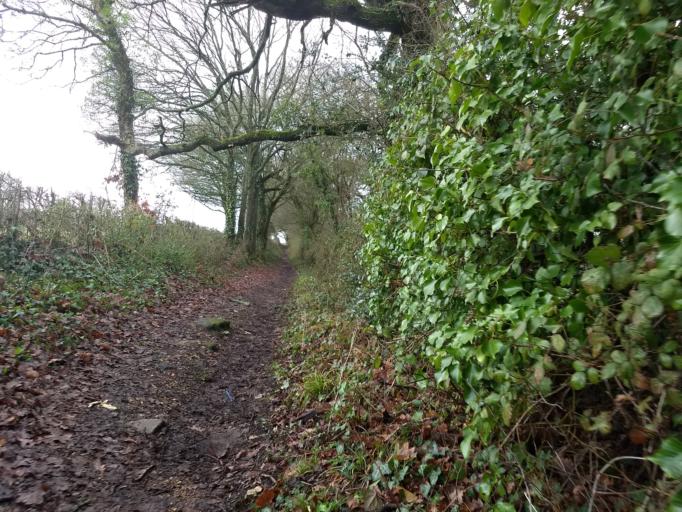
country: GB
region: England
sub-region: Isle of Wight
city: Newport
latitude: 50.7161
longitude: -1.2397
